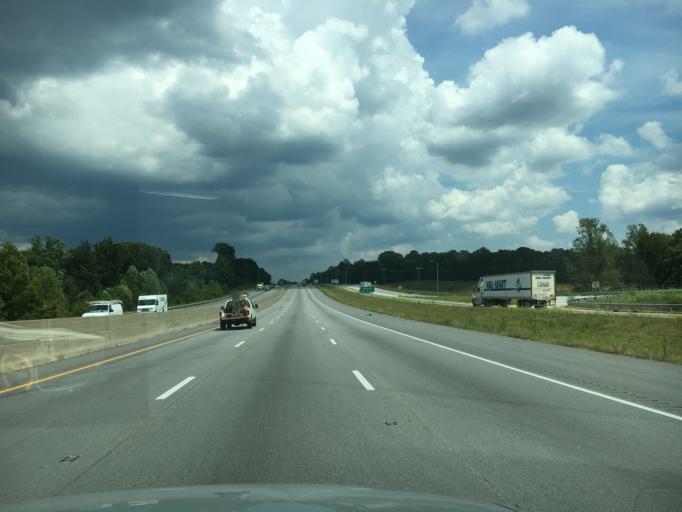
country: US
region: North Carolina
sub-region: Gaston County
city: Bessemer City
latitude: 35.2611
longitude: -81.2802
